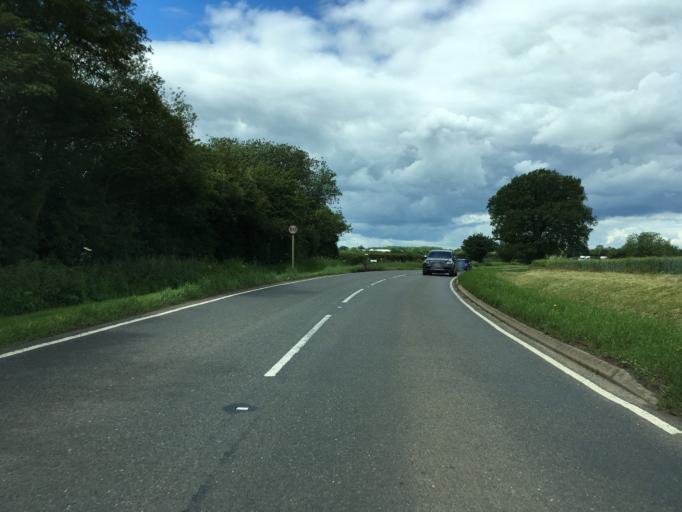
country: GB
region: England
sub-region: Northamptonshire
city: Brackley
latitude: 52.0770
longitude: -1.1319
